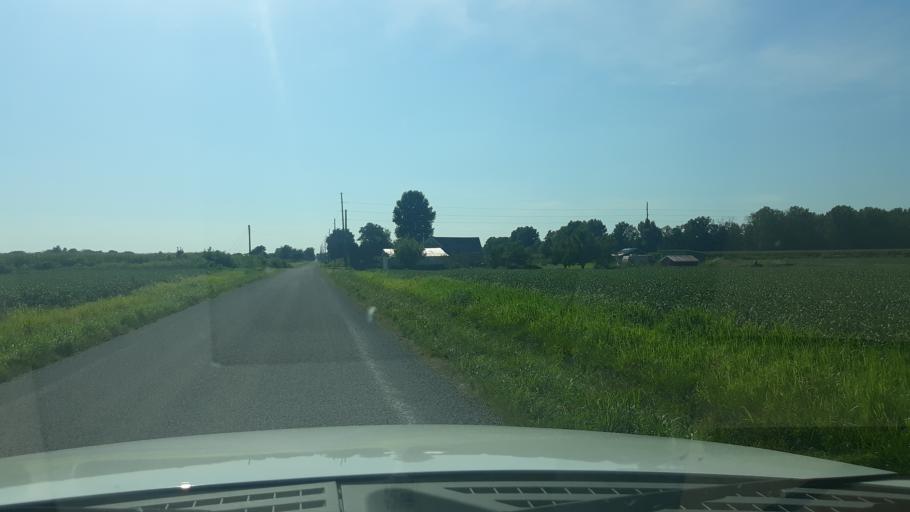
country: US
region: Illinois
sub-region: Saline County
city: Eldorado
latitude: 37.8630
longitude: -88.5024
